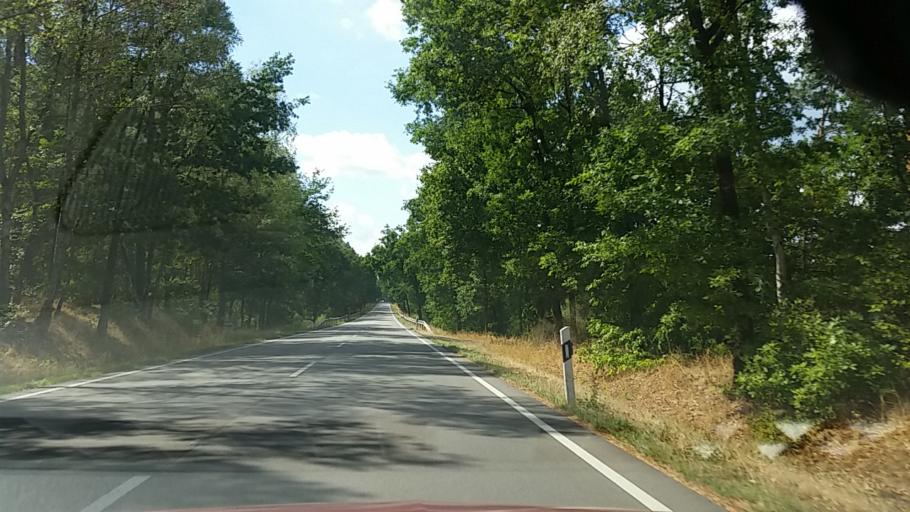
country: DE
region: Lower Saxony
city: Hankensbuttel
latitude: 52.7129
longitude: 10.5535
